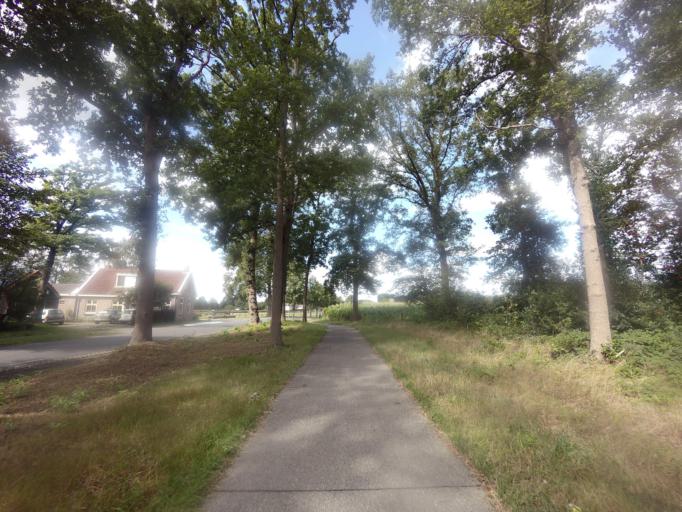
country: NL
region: Overijssel
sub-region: Gemeente Staphorst
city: Staphorst
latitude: 52.6643
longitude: 6.2641
